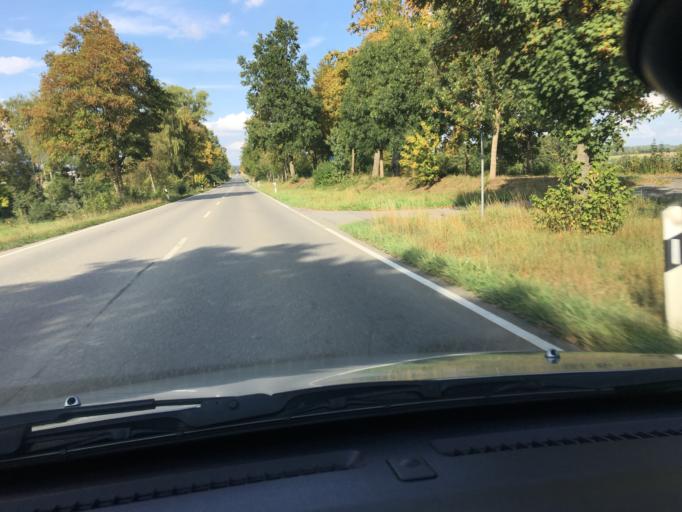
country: DE
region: Baden-Wuerttemberg
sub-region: Tuebingen Region
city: Bad Schussenried
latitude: 47.9867
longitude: 9.6499
